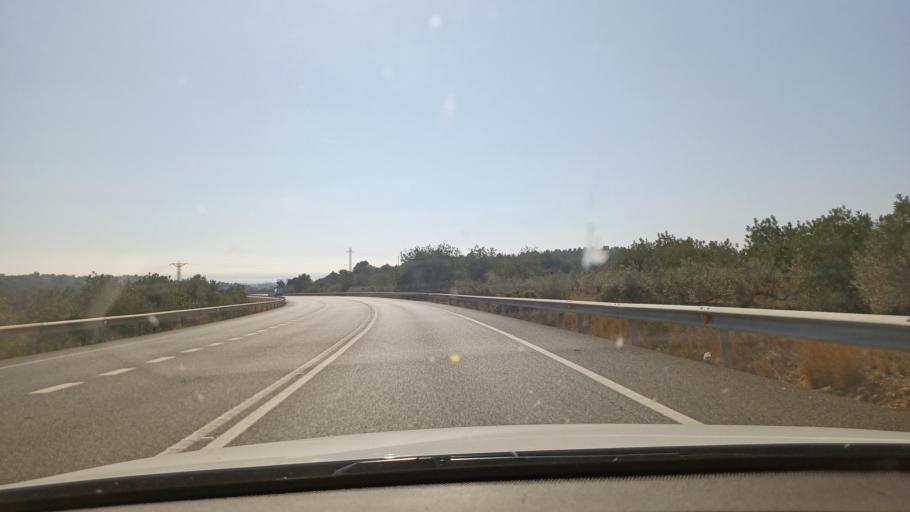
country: ES
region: Catalonia
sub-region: Provincia de Tarragona
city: El Perello
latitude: 40.8536
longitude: 0.7126
